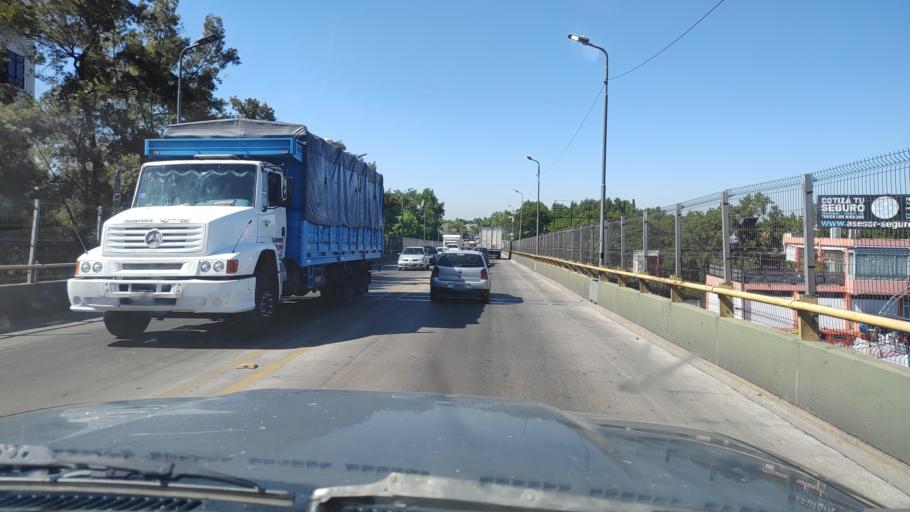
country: AR
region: Buenos Aires
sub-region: Partido de Moron
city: Moron
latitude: -34.6495
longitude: -58.6290
